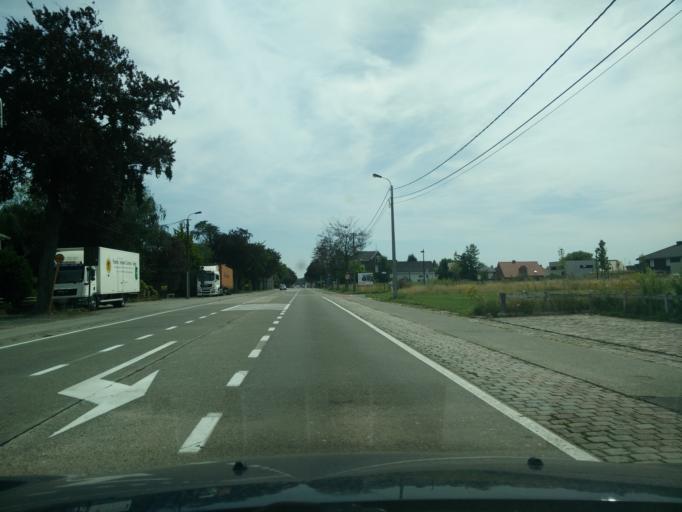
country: BE
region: Flanders
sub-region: Provincie Oost-Vlaanderen
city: Melle
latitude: 51.0187
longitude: 3.7804
